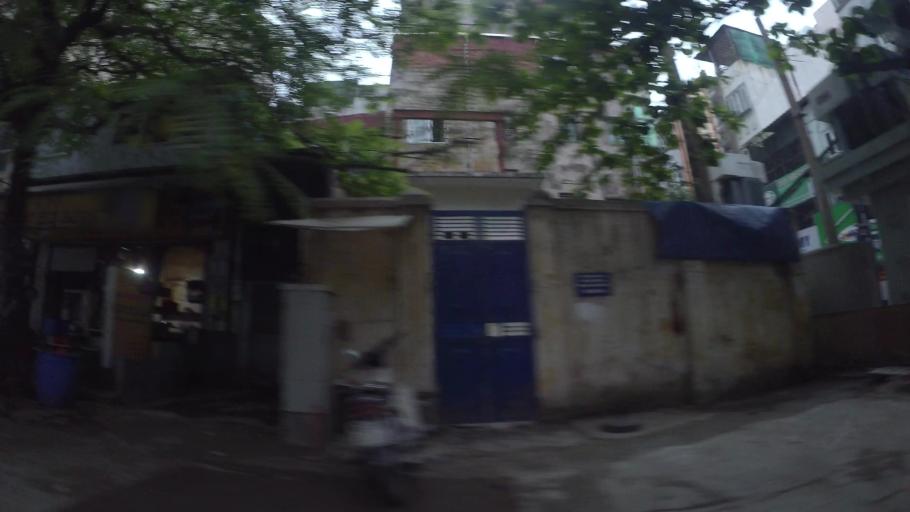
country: VN
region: Ha Noi
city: Hai BaTrung
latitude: 20.9872
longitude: 105.8513
